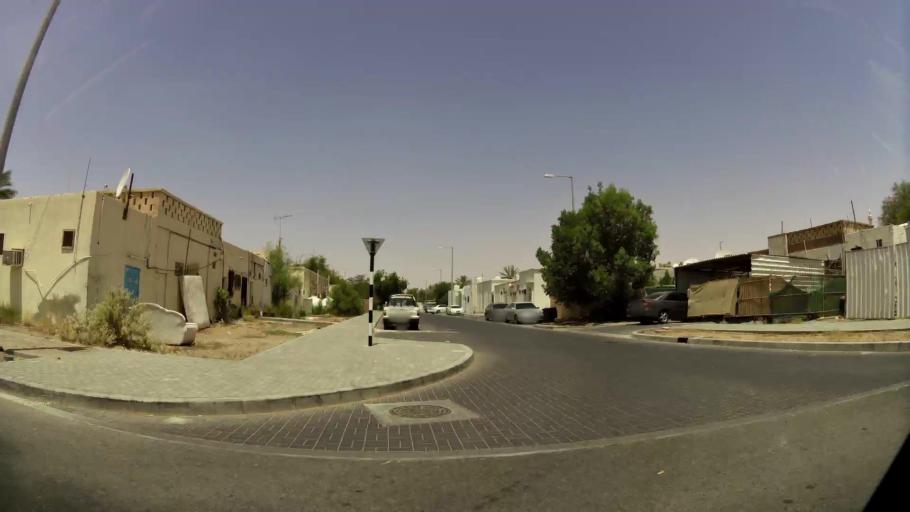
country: OM
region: Al Buraimi
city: Al Buraymi
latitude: 24.2709
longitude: 55.7431
